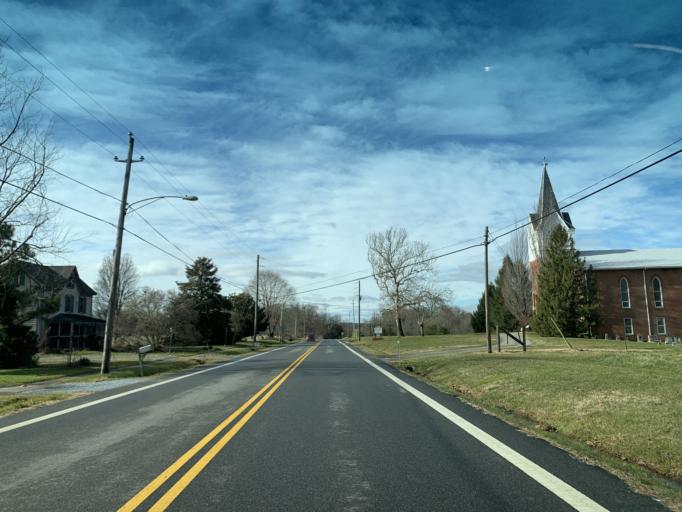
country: US
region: Maryland
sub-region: Kent County
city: Chestertown
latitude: 39.3281
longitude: -76.0498
